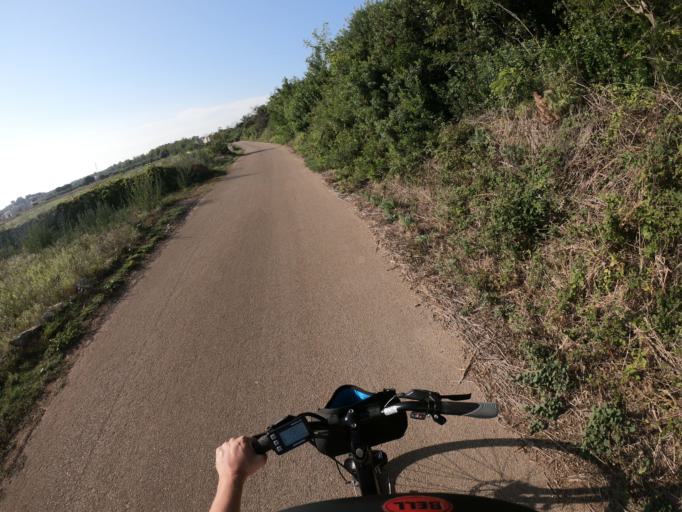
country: IT
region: Apulia
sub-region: Provincia di Lecce
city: Leuca
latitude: 39.8152
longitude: 18.3623
